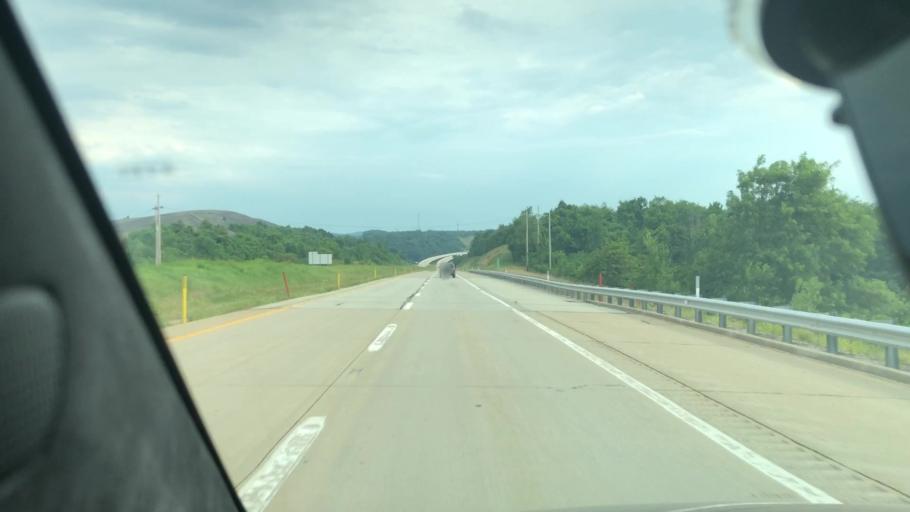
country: US
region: Pennsylvania
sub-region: Washington County
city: Baidland
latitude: 40.2236
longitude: -79.9855
